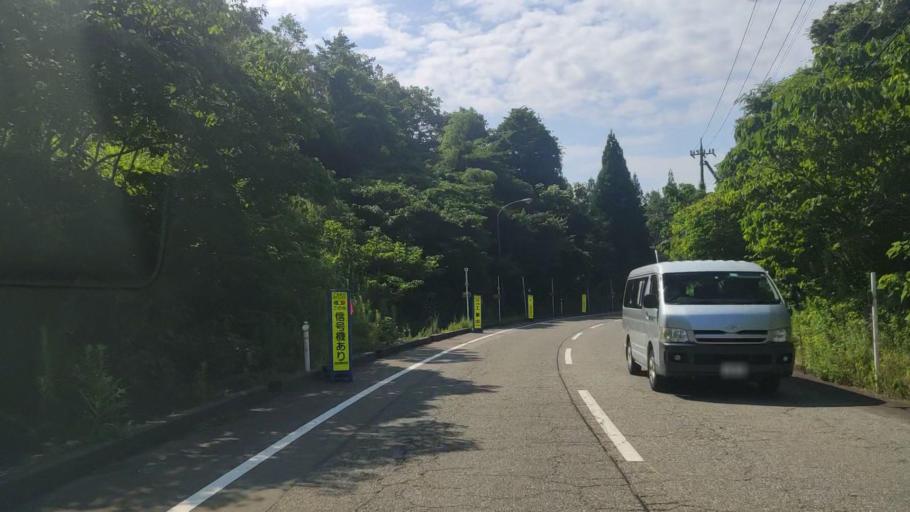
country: JP
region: Ishikawa
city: Komatsu
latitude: 36.3829
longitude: 136.4973
